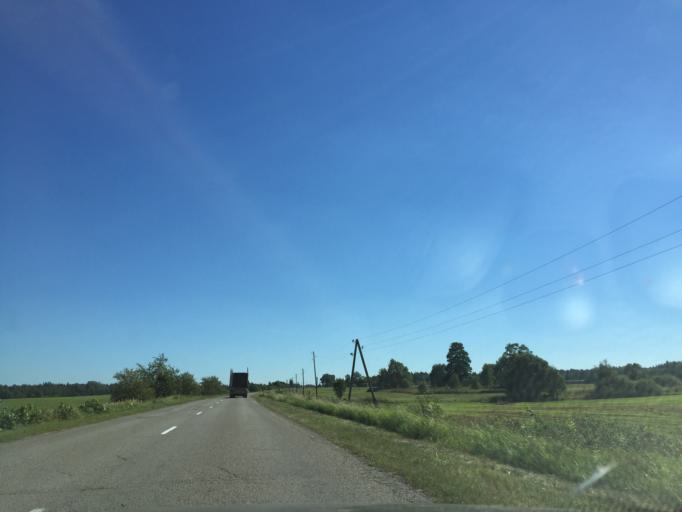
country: LV
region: Akniste
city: Akniste
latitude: 56.1056
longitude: 25.8559
